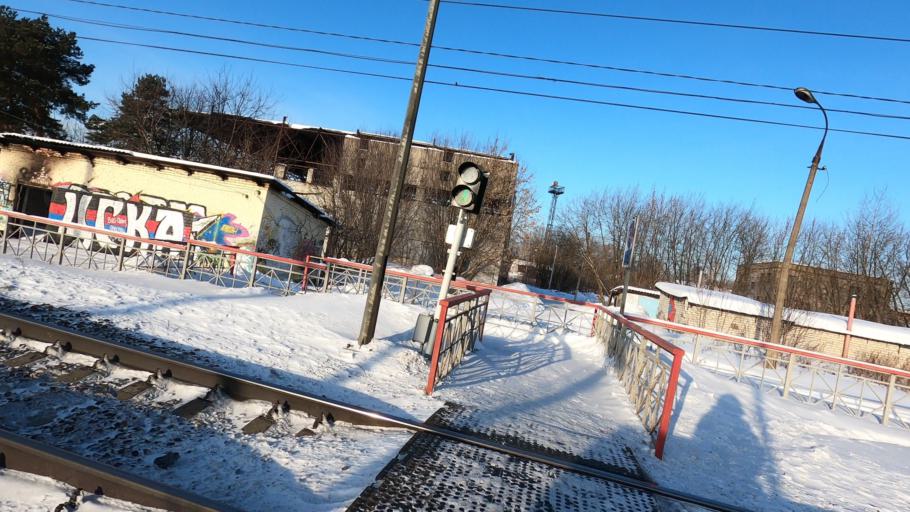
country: RU
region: Moskovskaya
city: Pavlovskiy Posad
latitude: 55.7731
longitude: 38.6970
